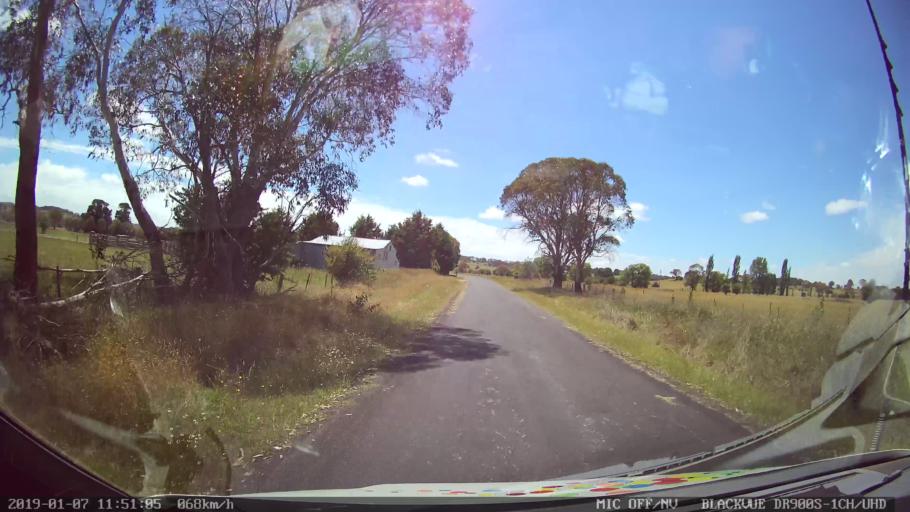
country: AU
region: New South Wales
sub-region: Guyra
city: Guyra
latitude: -30.3093
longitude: 151.6425
